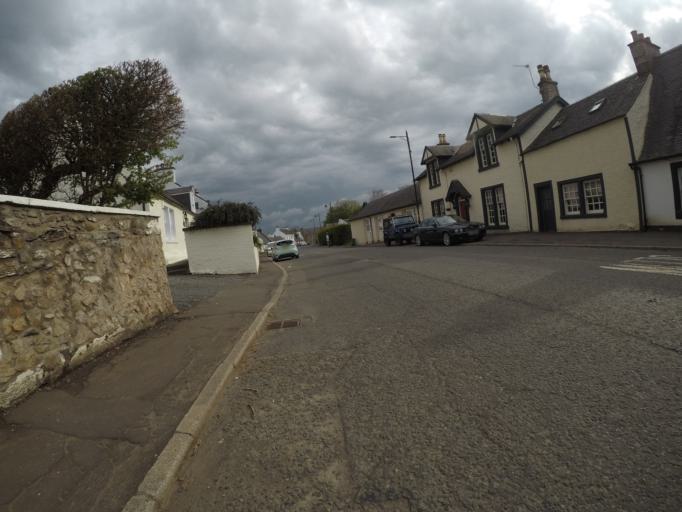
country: GB
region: Scotland
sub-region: East Ayrshire
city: Kilmarnock
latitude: 55.6555
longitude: -4.4456
